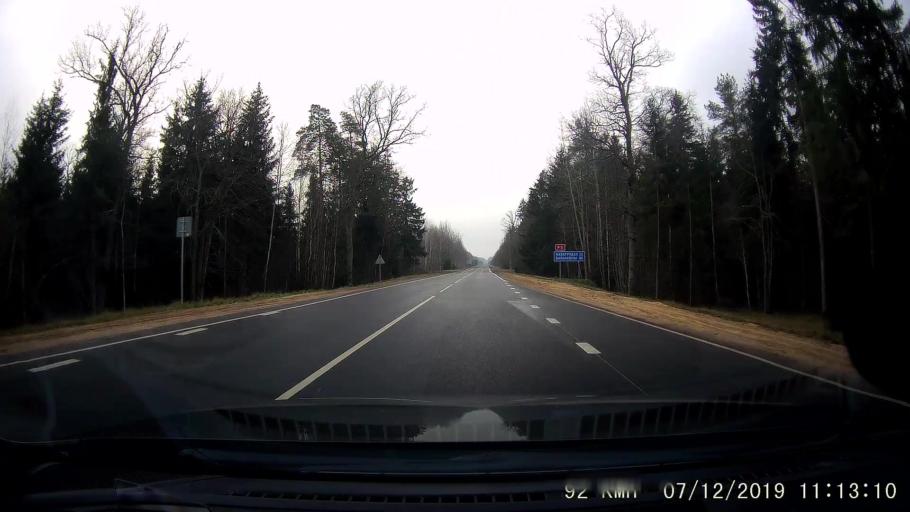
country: BY
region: Grodnenskaya
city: Iwye
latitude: 53.8782
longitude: 25.7397
